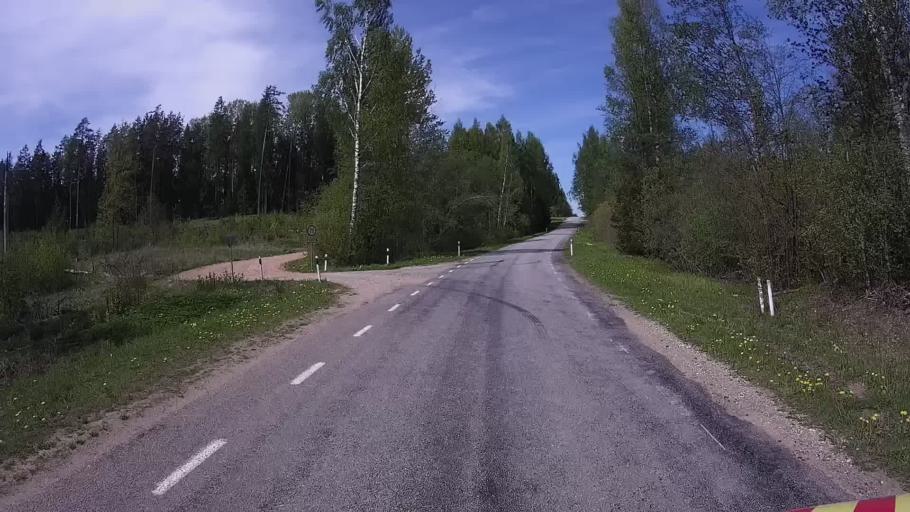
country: EE
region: Vorumaa
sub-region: Antsla vald
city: Vana-Antsla
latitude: 57.6234
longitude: 26.3477
